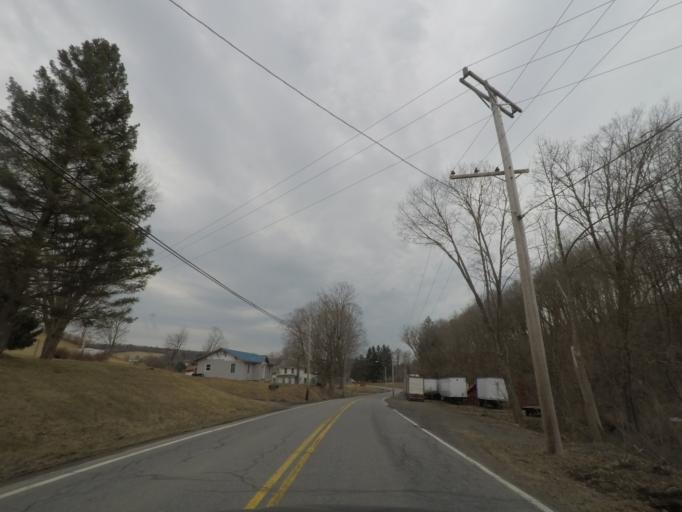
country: US
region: New York
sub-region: Washington County
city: Greenwich
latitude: 43.0785
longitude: -73.4955
